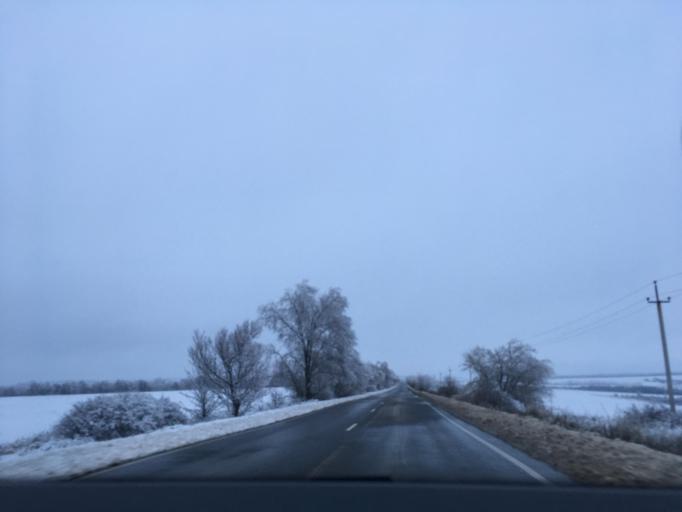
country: RU
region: Voronezj
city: Verkhniy Mamon
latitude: 50.0200
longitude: 40.1126
